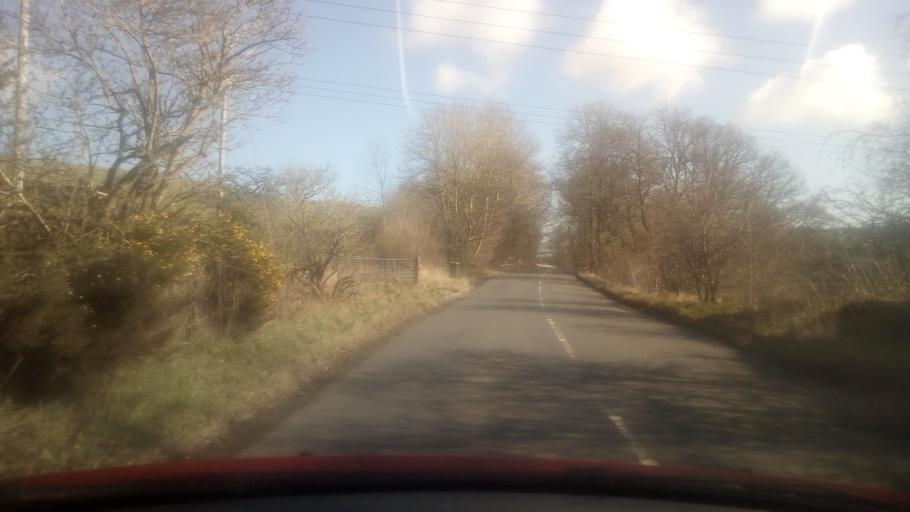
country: GB
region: Scotland
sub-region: The Scottish Borders
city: Selkirk
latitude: 55.5601
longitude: -2.8429
